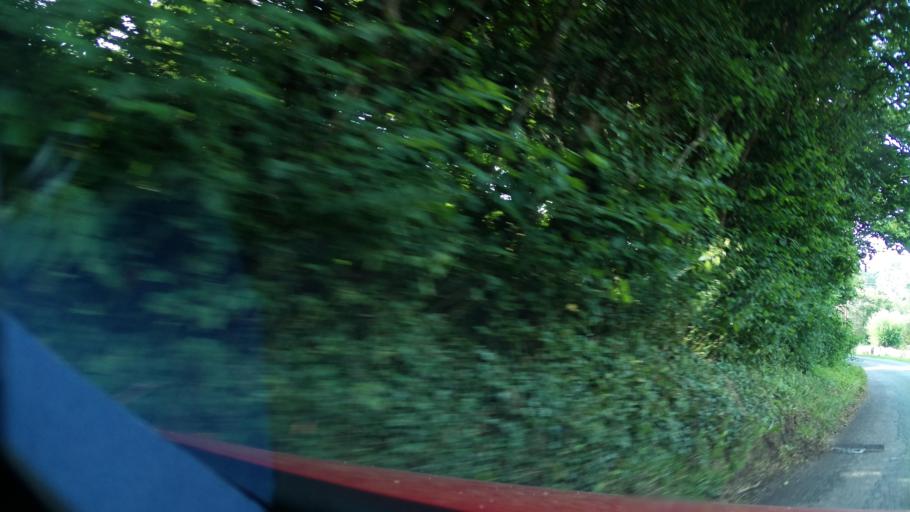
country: GB
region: England
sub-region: Bath and North East Somerset
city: East Harptree
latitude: 51.2828
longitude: -2.5872
